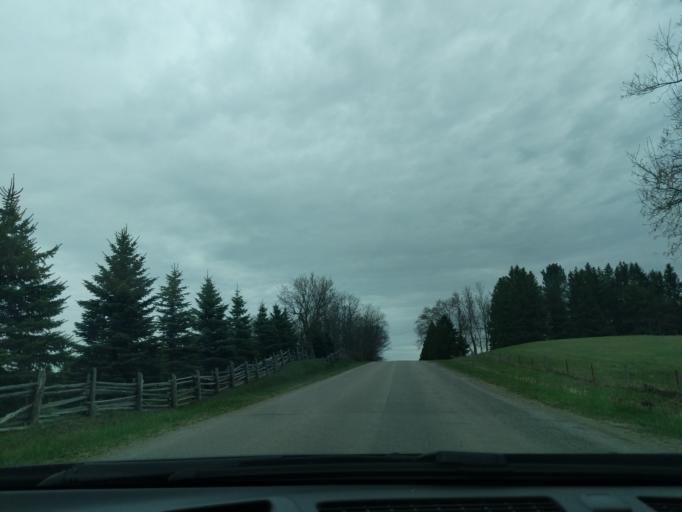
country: CA
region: Ontario
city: Orangeville
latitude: 44.0127
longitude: -79.9668
